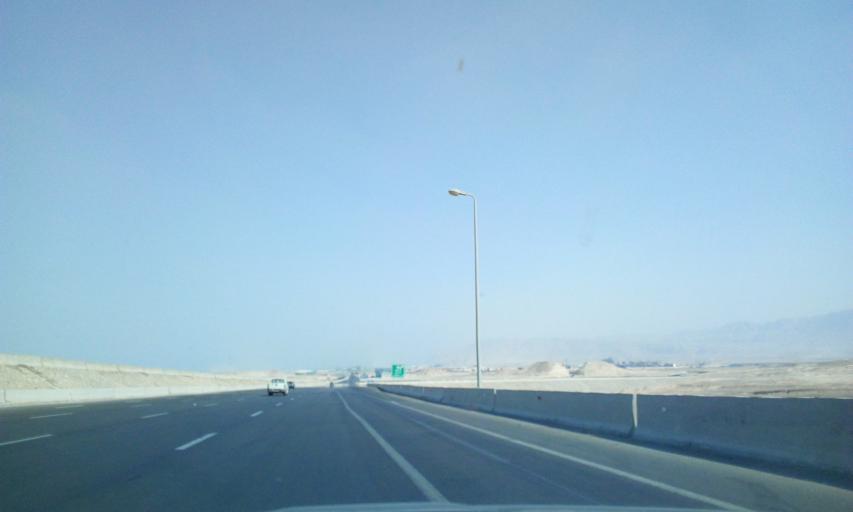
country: EG
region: As Suways
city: Ain Sukhna
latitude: 29.6749
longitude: 32.2295
